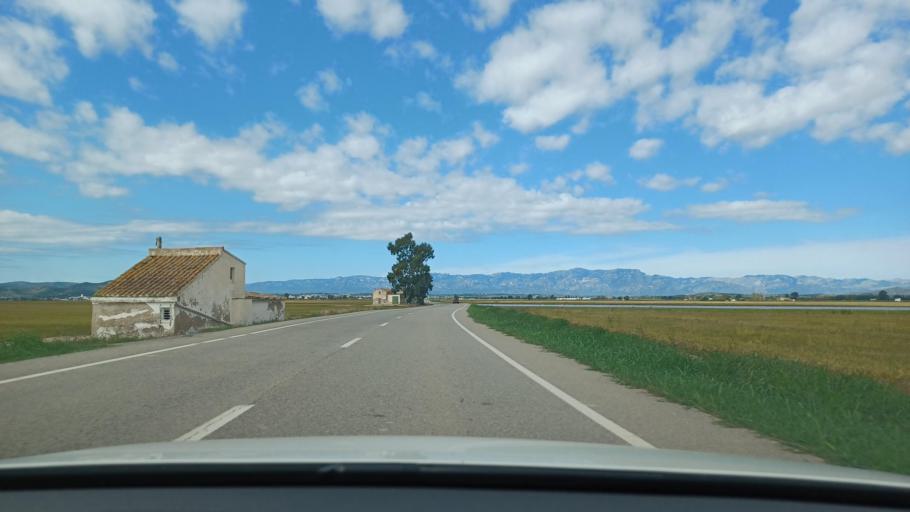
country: ES
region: Catalonia
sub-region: Provincia de Tarragona
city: Deltebre
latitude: 40.7031
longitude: 0.6621
